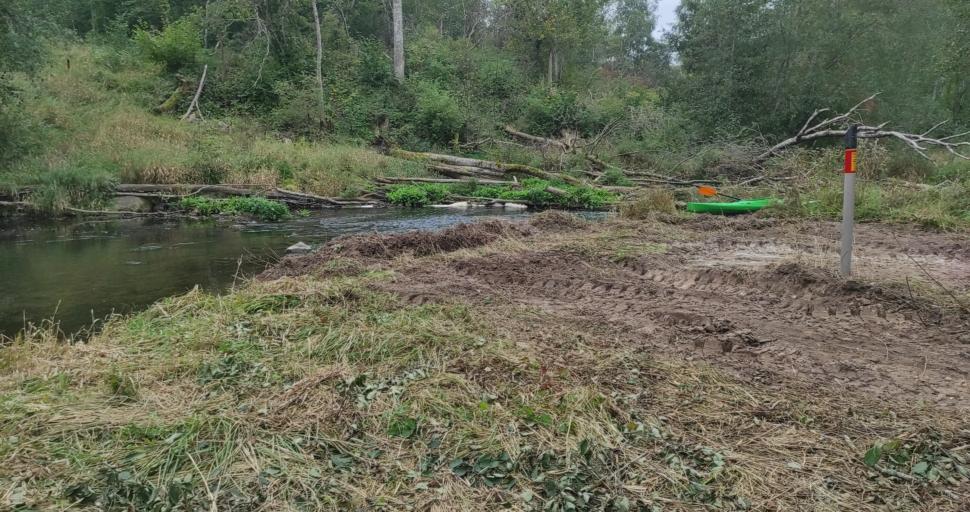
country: LV
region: Skrunda
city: Skrunda
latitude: 56.7015
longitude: 22.1999
